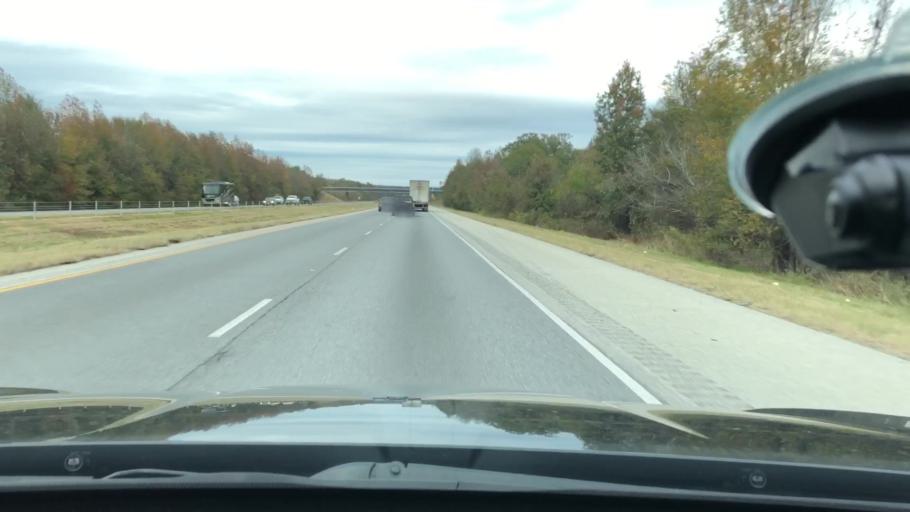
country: US
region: Arkansas
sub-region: Clark County
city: Arkadelphia
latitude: 34.1683
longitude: -93.0754
